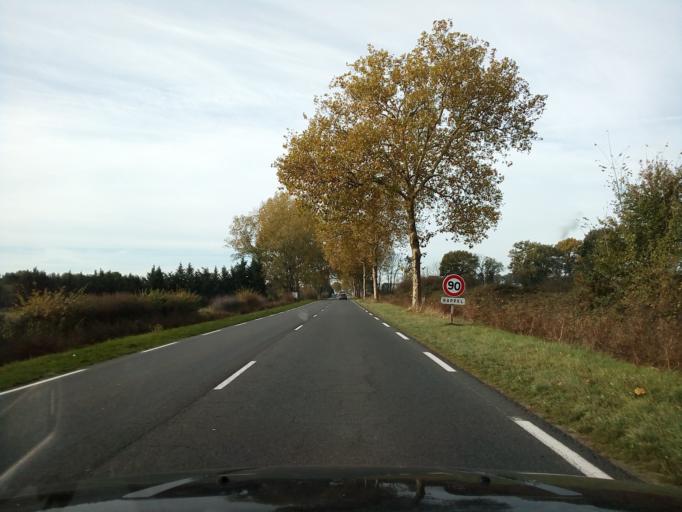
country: FR
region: Auvergne
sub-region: Departement de l'Allier
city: Saint-Pourcain-sur-Sioule
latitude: 46.3171
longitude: 3.3321
